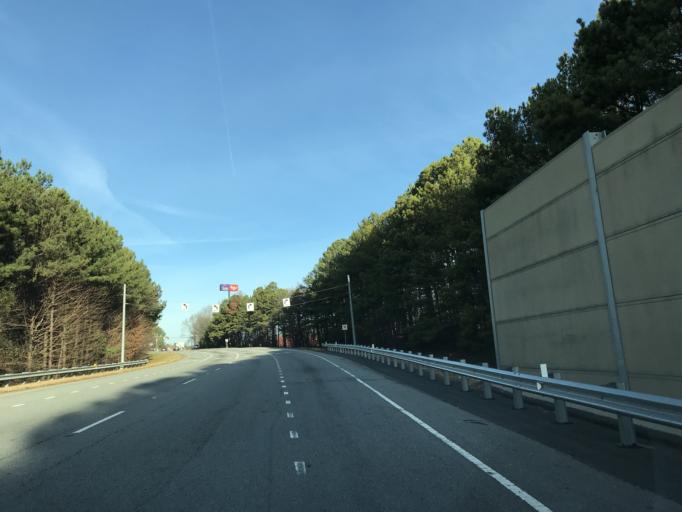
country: US
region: Georgia
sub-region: Cobb County
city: Kennesaw
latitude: 34.0534
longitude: -84.5910
